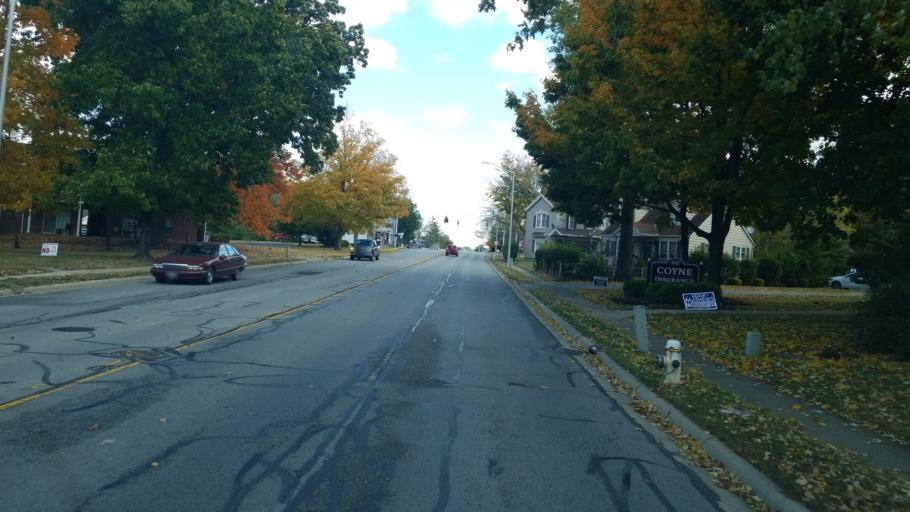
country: US
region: Ohio
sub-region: Warren County
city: Lebanon
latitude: 39.4377
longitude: -84.1996
